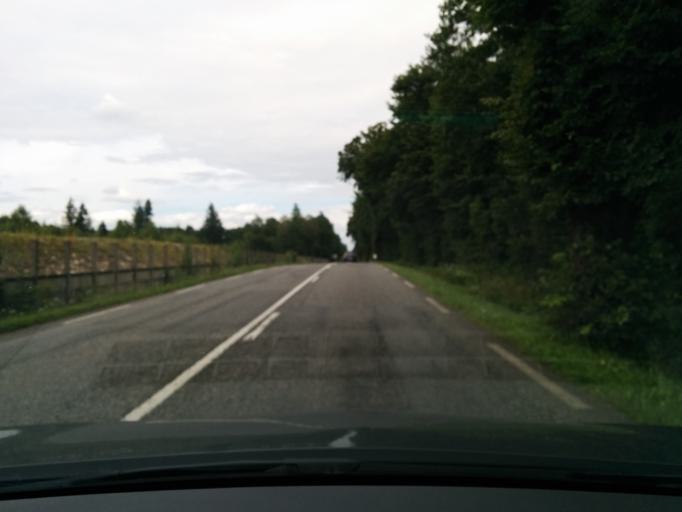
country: FR
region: Midi-Pyrenees
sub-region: Departement des Hautes-Pyrenees
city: La Barthe-de-Neste
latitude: 43.0942
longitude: 0.3924
